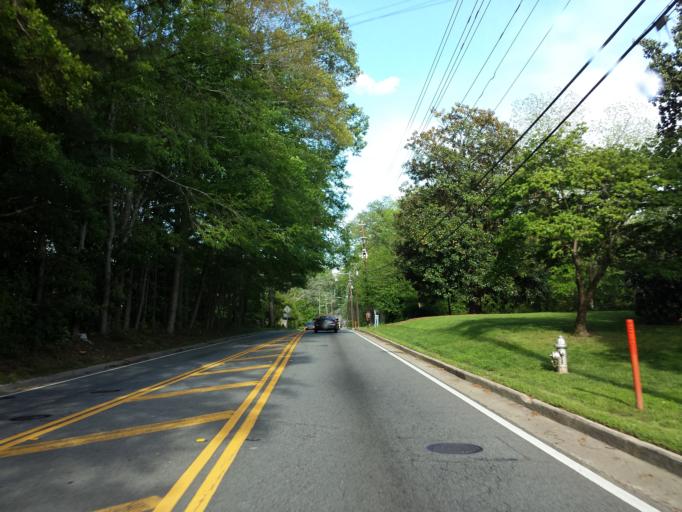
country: US
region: Georgia
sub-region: Cobb County
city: Marietta
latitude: 33.9519
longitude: -84.5670
